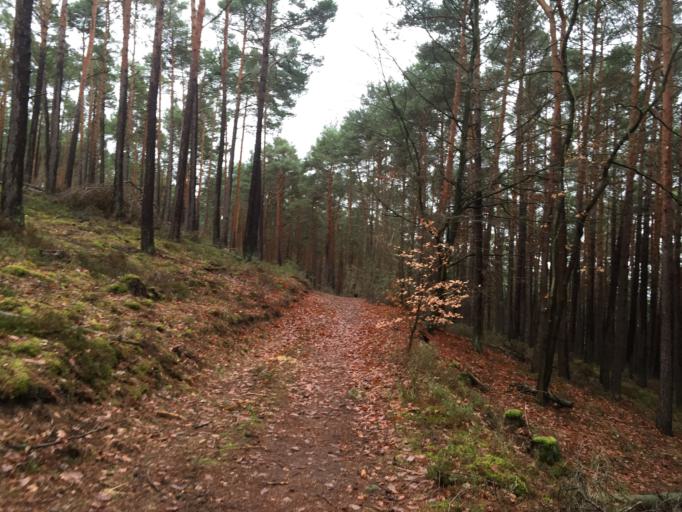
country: DE
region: Rheinland-Pfalz
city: Altleiningen
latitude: 49.5066
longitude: 8.0817
